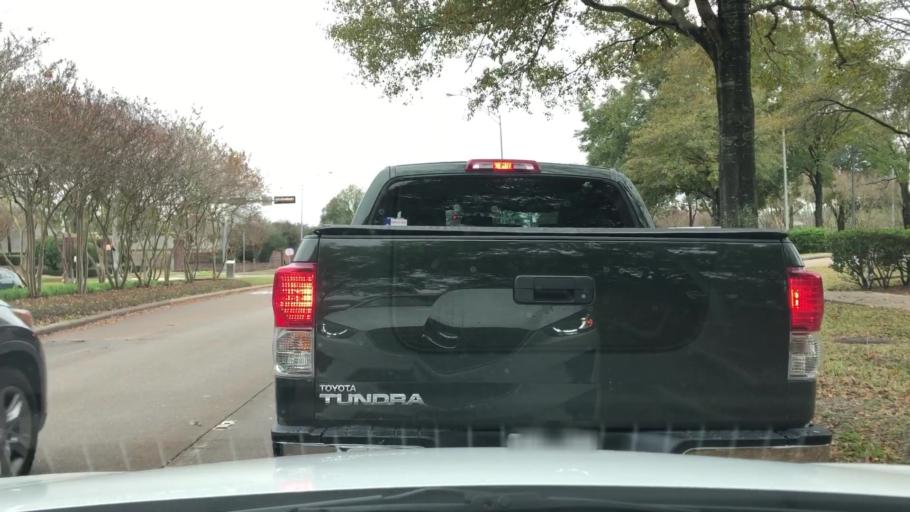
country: US
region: Texas
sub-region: Fort Bend County
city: Cinco Ranch
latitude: 29.7412
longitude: -95.7513
